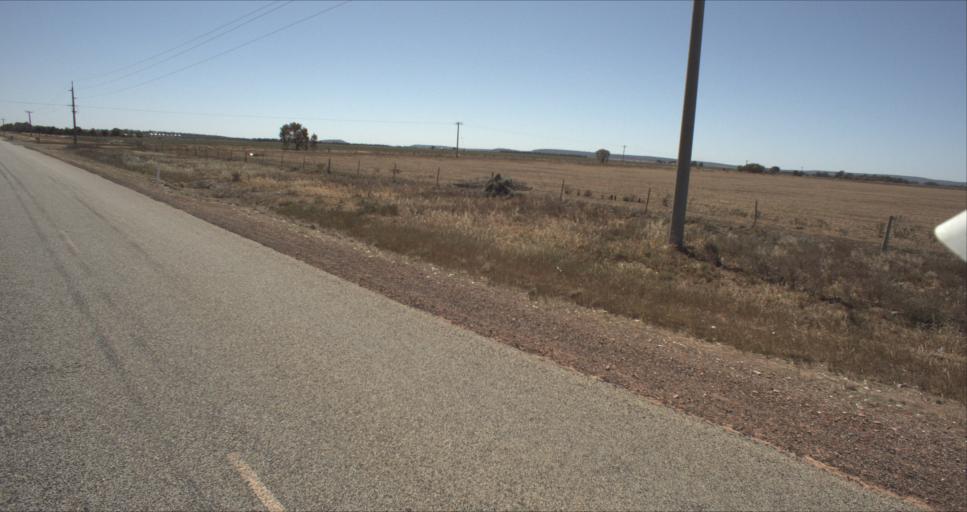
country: AU
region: New South Wales
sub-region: Leeton
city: Leeton
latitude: -34.4588
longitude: 146.2946
